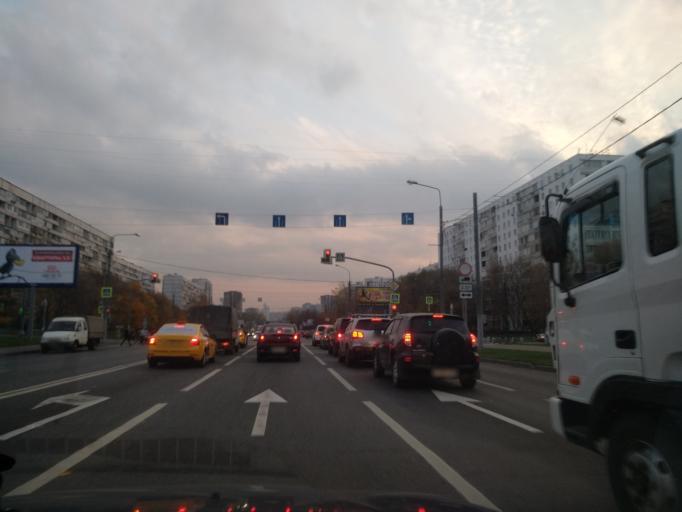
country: RU
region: Moscow
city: Vatutino
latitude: 55.8754
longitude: 37.6673
